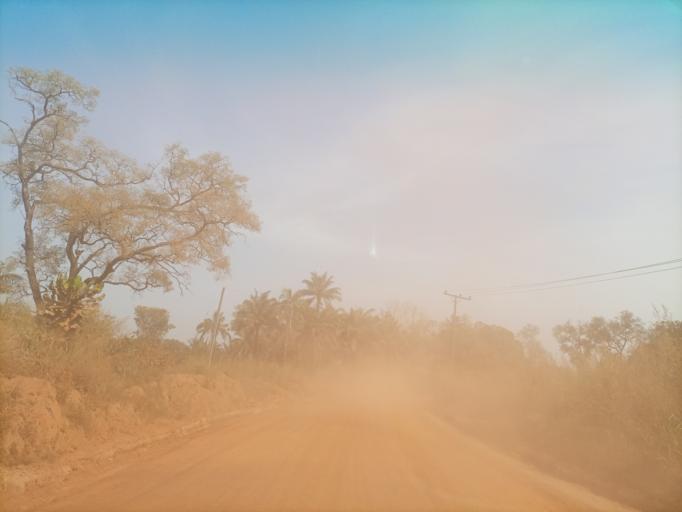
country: NG
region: Enugu
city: Eha Amufu
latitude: 6.6682
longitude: 7.7514
